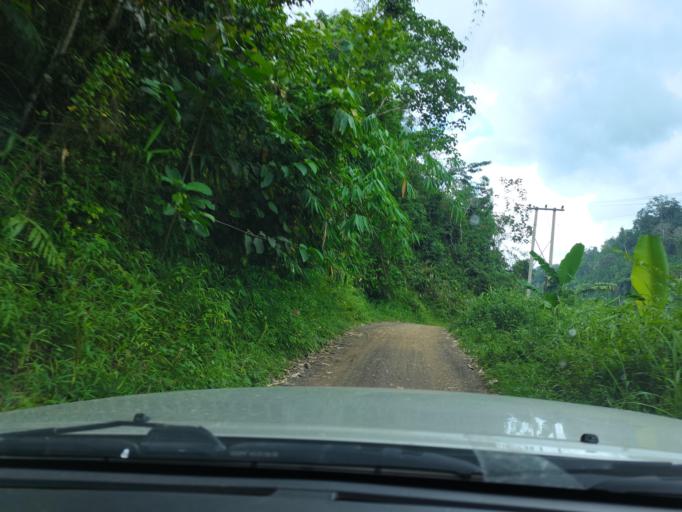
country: LA
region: Loungnamtha
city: Muang Long
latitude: 20.7666
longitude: 101.0181
